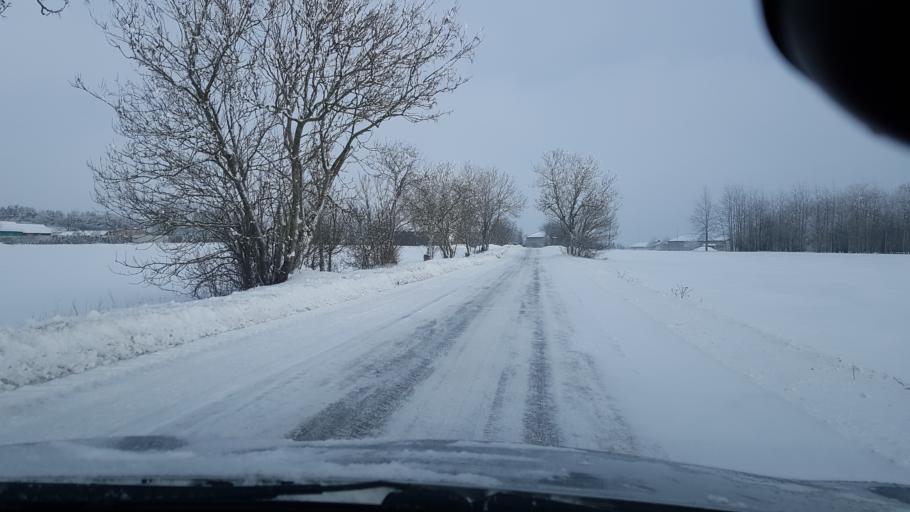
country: EE
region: Harju
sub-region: Keila linn
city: Keila
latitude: 59.3346
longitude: 24.4470
